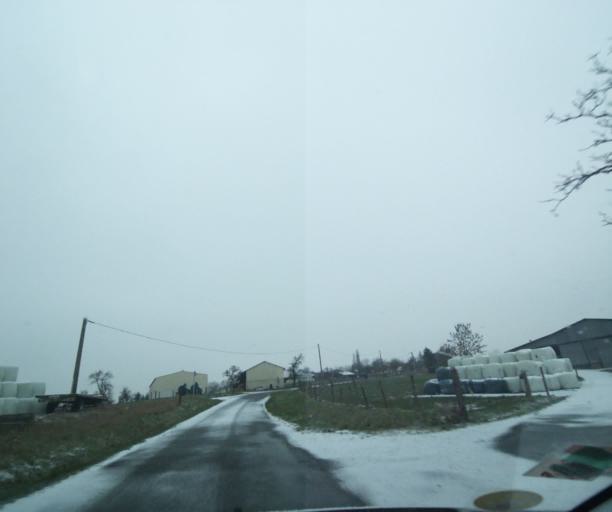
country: FR
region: Champagne-Ardenne
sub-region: Departement de la Haute-Marne
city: Wassy
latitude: 48.4764
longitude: 5.0381
